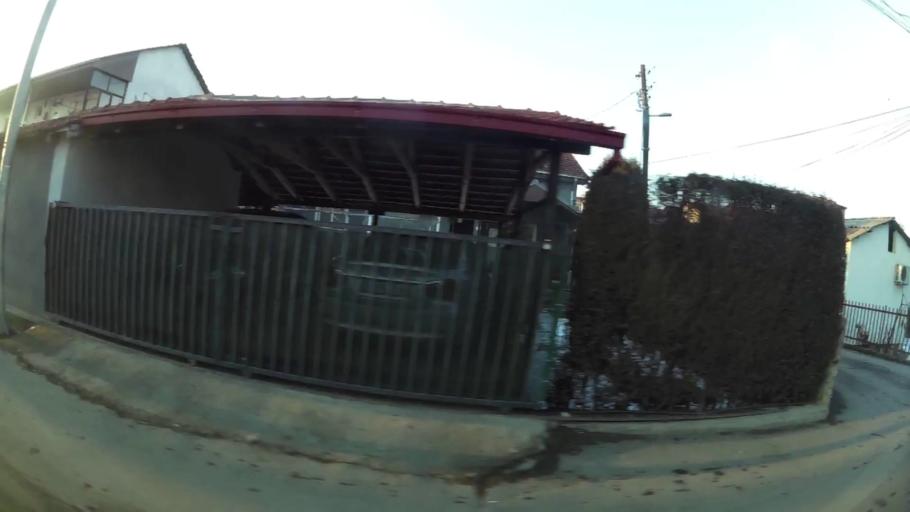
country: MK
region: Kisela Voda
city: Kisela Voda
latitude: 41.9761
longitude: 21.4917
